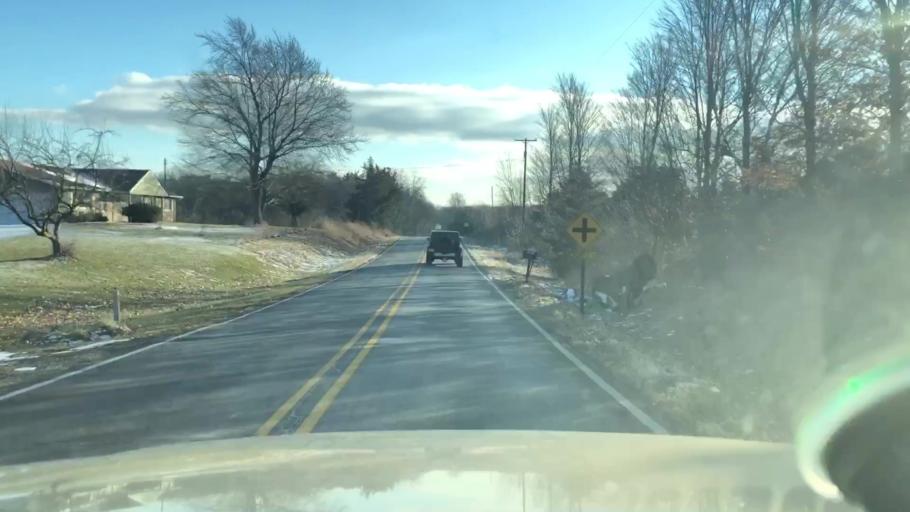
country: US
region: Michigan
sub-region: Jackson County
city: Vandercook Lake
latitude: 42.1188
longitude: -84.4514
